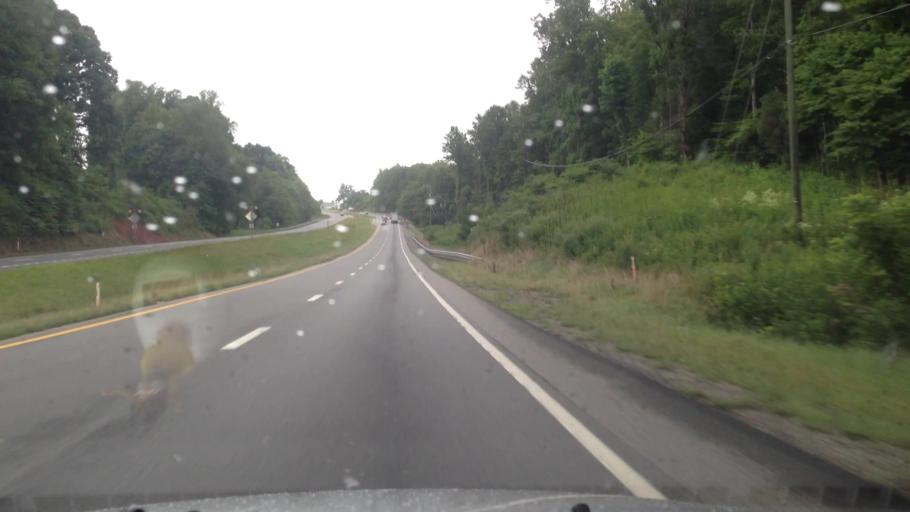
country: US
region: Virginia
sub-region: Henry County
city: Stanleytown
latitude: 36.7841
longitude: -79.9362
